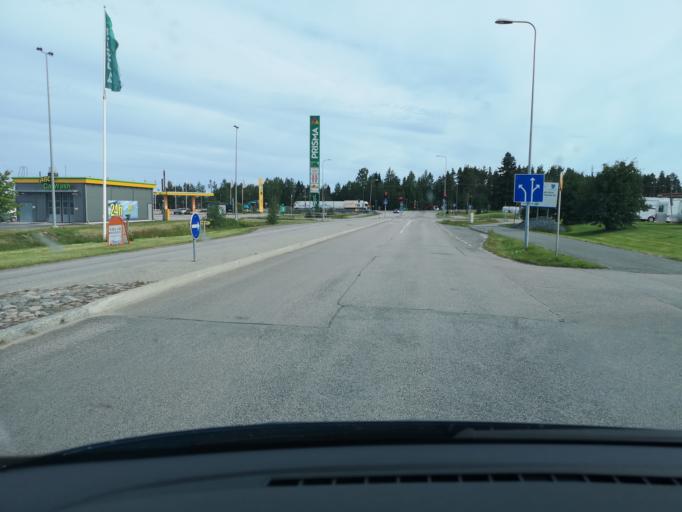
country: FI
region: Northern Ostrobothnia
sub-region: Ylivieska
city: Ylivieska
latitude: 64.0617
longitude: 24.5597
